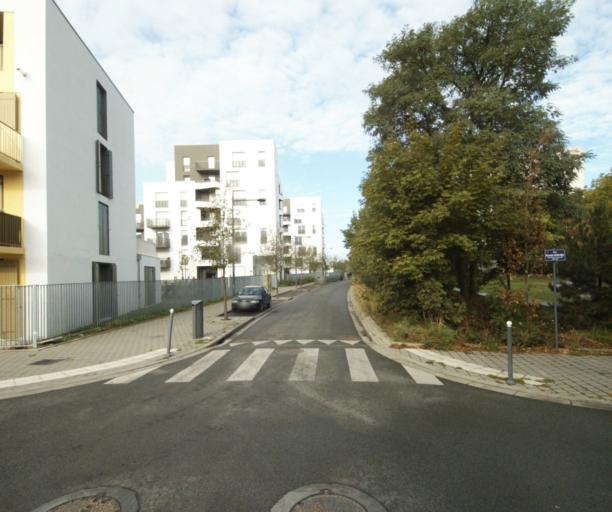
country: FR
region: Nord-Pas-de-Calais
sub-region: Departement du Nord
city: Wattignies
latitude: 50.6034
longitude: 3.0472
